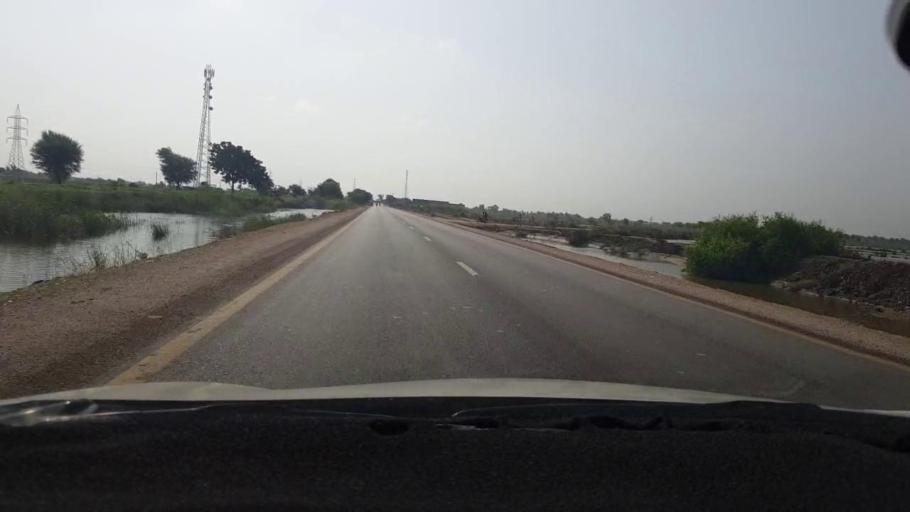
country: PK
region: Sindh
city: Jhol
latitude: 25.8873
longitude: 69.0332
